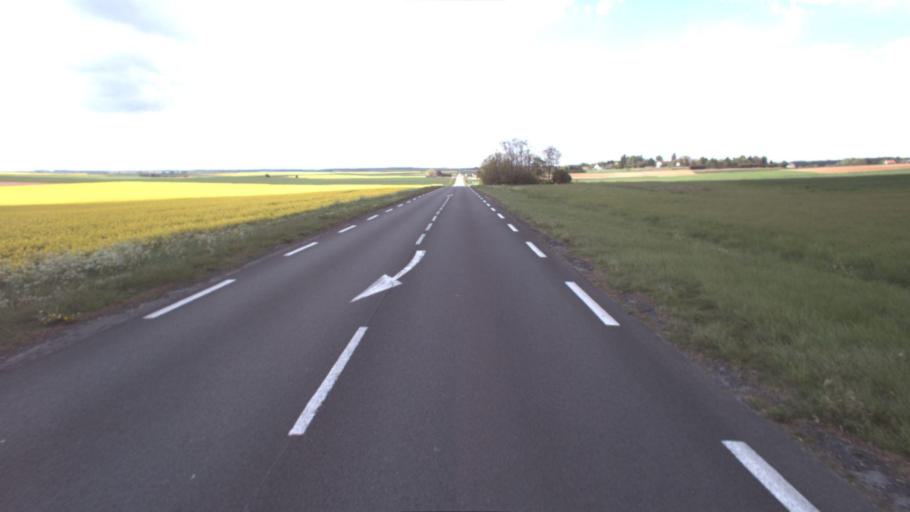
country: FR
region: Ile-de-France
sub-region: Departement de Seine-et-Marne
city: Villiers-Saint-Georges
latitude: 48.6921
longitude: 3.4101
